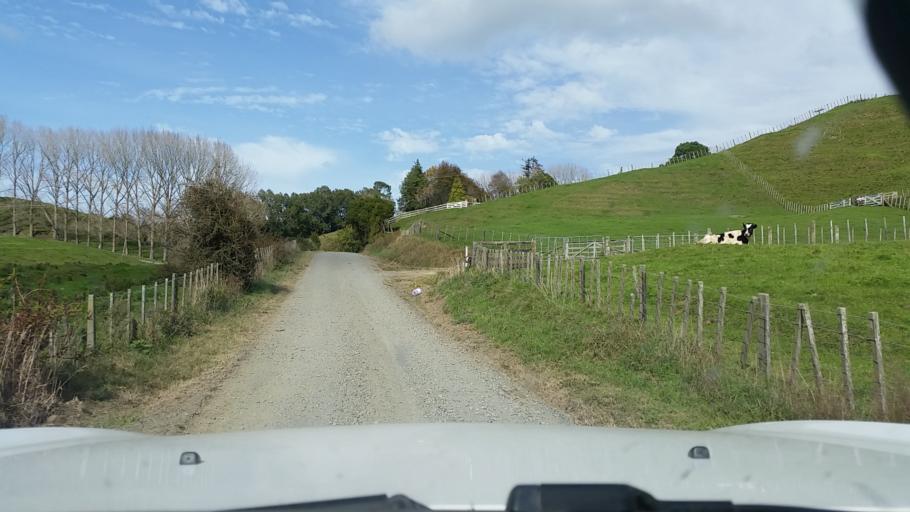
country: NZ
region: Waikato
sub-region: Matamata-Piako District
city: Matamata
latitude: -37.8235
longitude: 175.6753
